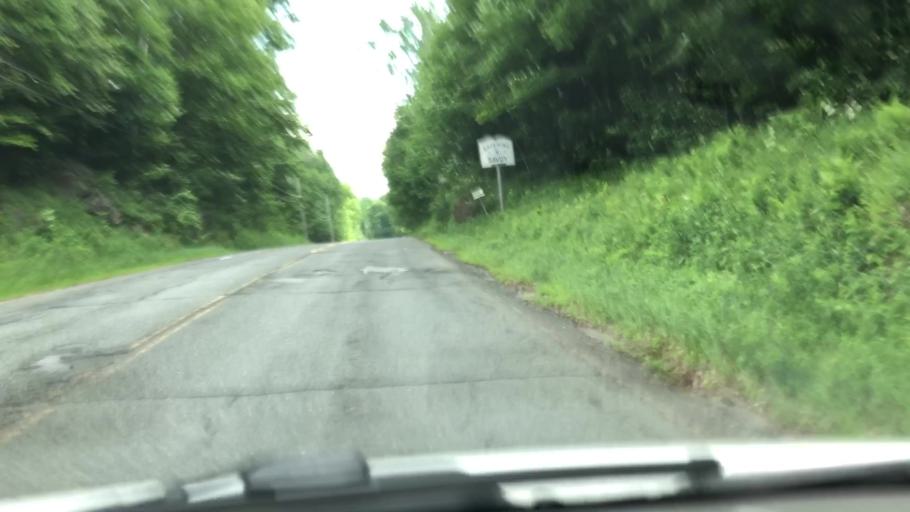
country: US
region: Massachusetts
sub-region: Berkshire County
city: Adams
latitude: 42.5845
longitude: -73.0827
